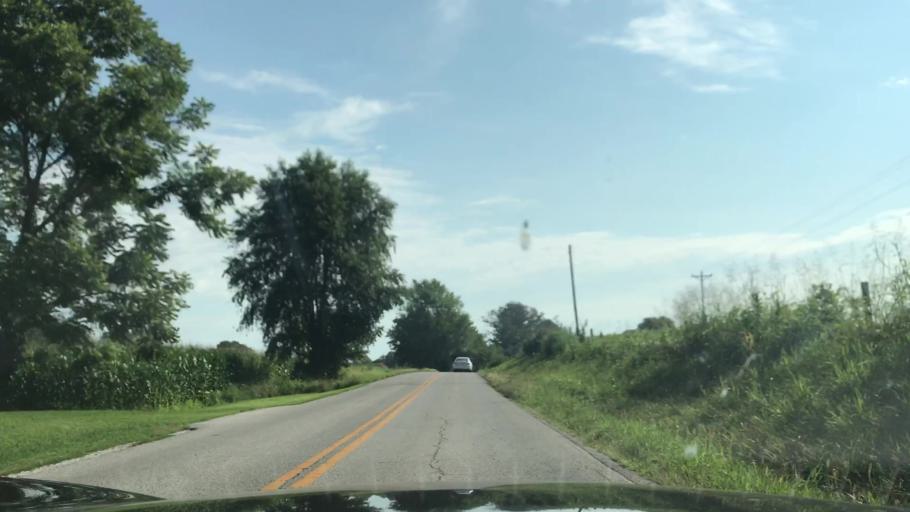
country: US
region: Kentucky
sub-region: Hart County
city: Munfordville
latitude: 37.2059
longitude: -85.7434
